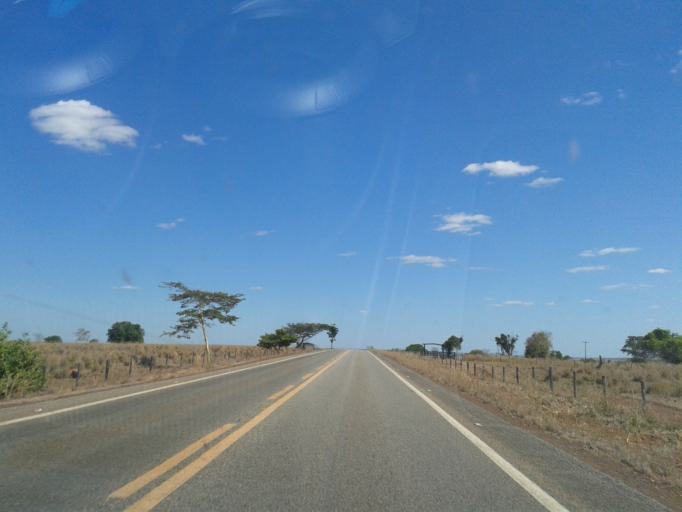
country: BR
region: Goias
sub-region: Sao Miguel Do Araguaia
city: Sao Miguel do Araguaia
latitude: -13.4138
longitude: -50.2682
